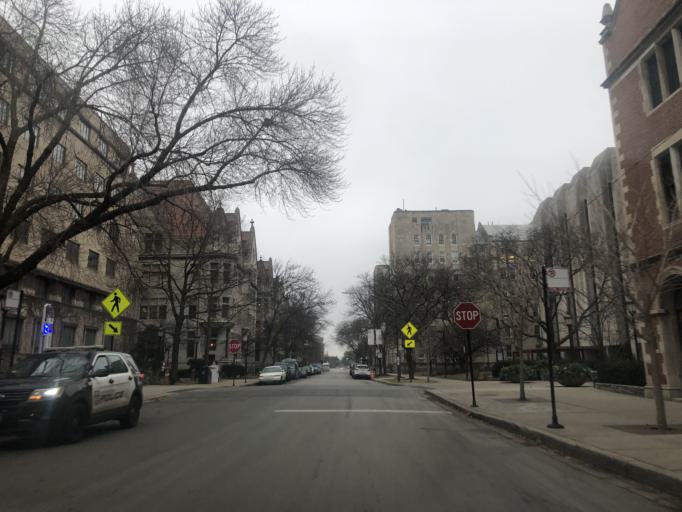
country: US
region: Illinois
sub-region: Cook County
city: Chicago
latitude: 41.7899
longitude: -87.6013
